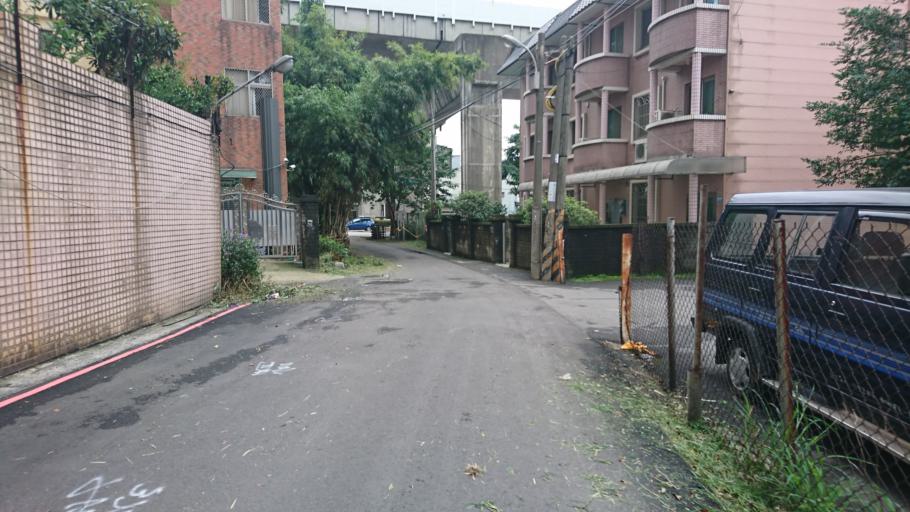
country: TW
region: Taiwan
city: Taoyuan City
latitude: 25.0597
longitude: 121.2952
